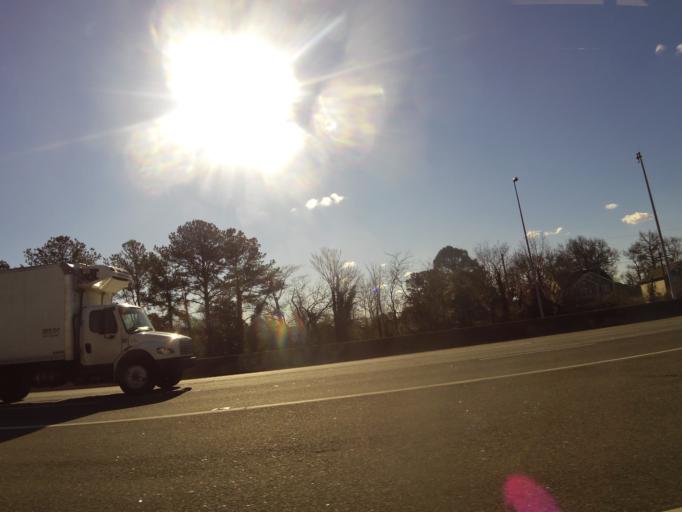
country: US
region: Virginia
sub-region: City of Portsmouth
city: Portsmouth
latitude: 36.8280
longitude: -76.3218
